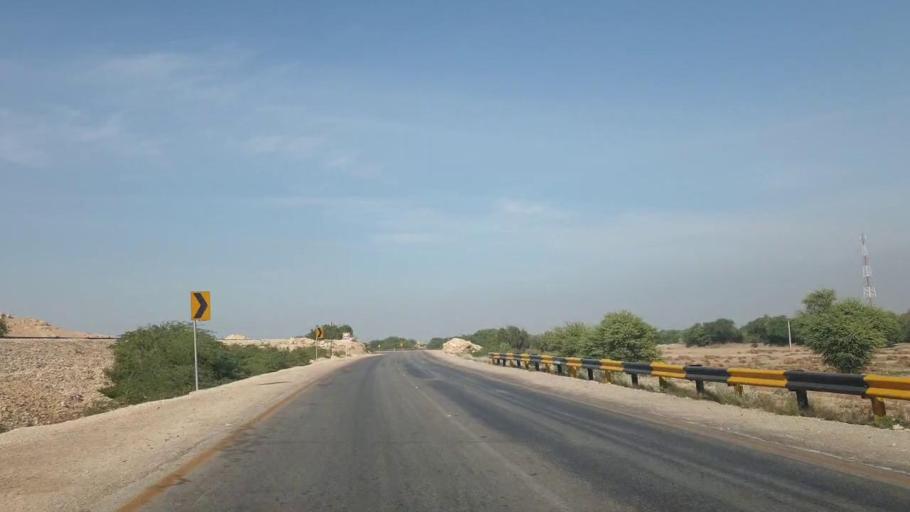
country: PK
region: Sindh
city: Sehwan
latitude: 26.2970
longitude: 67.8946
